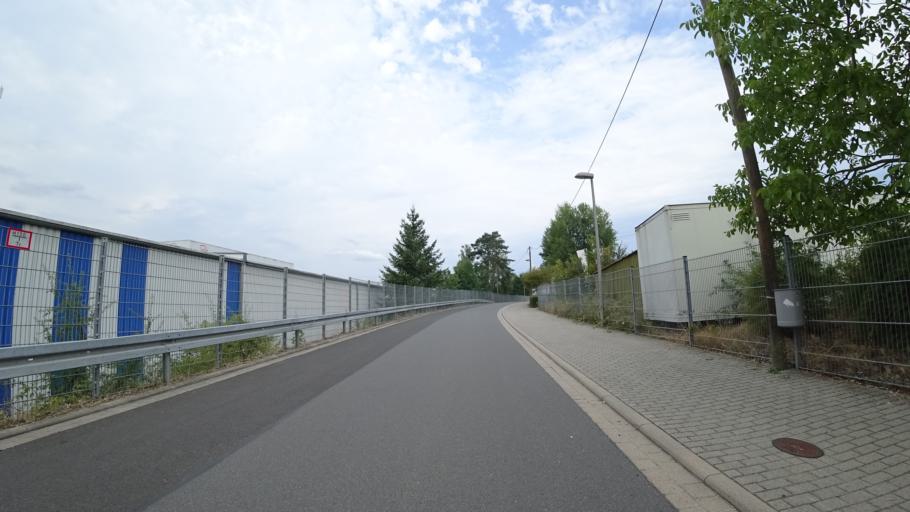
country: DE
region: Bavaria
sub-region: Regierungsbezirk Unterfranken
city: Miltenberg
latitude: 49.7076
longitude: 9.2455
